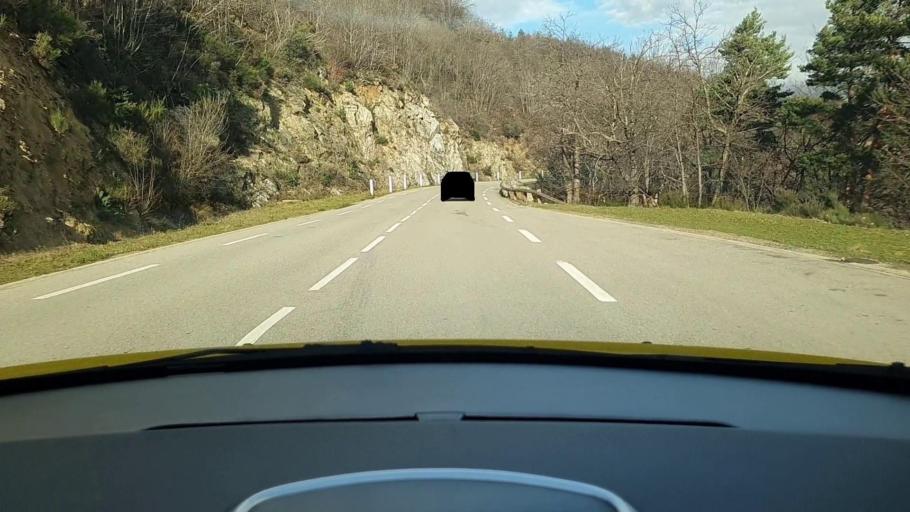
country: FR
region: Languedoc-Roussillon
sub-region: Departement du Gard
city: Branoux-les-Taillades
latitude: 44.3982
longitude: 3.9336
